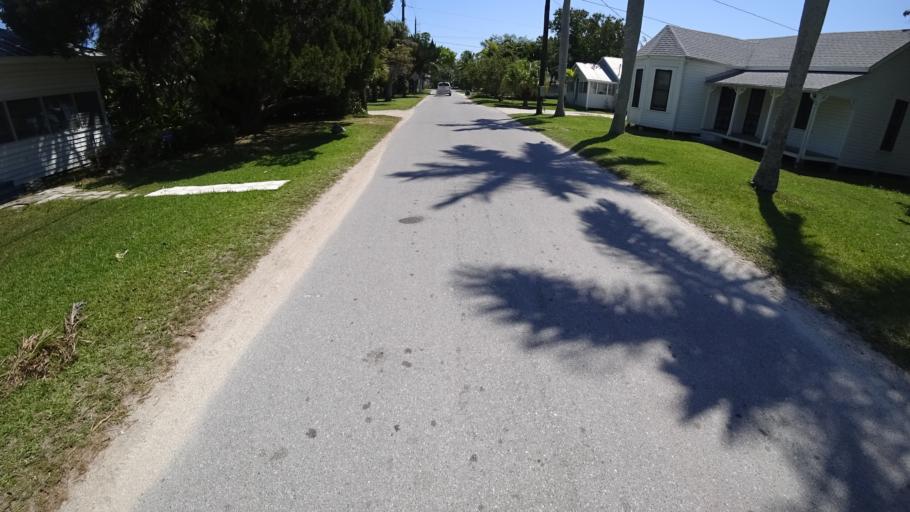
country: US
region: Florida
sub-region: Manatee County
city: Cortez
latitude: 27.4676
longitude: -82.6821
